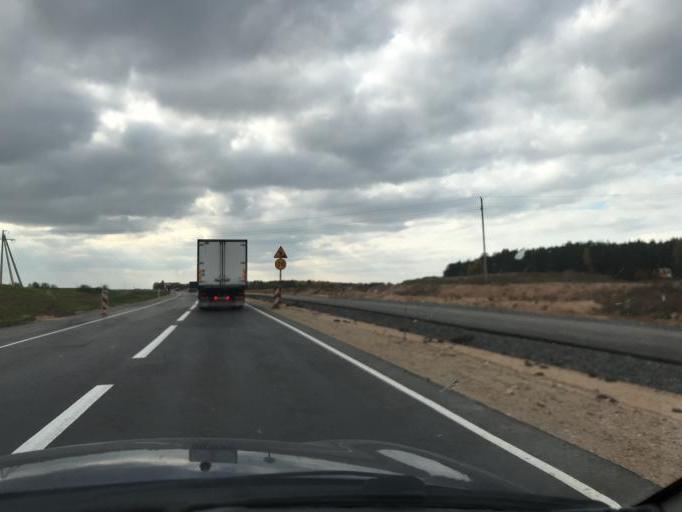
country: BY
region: Grodnenskaya
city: Lida
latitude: 53.8234
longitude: 25.1266
